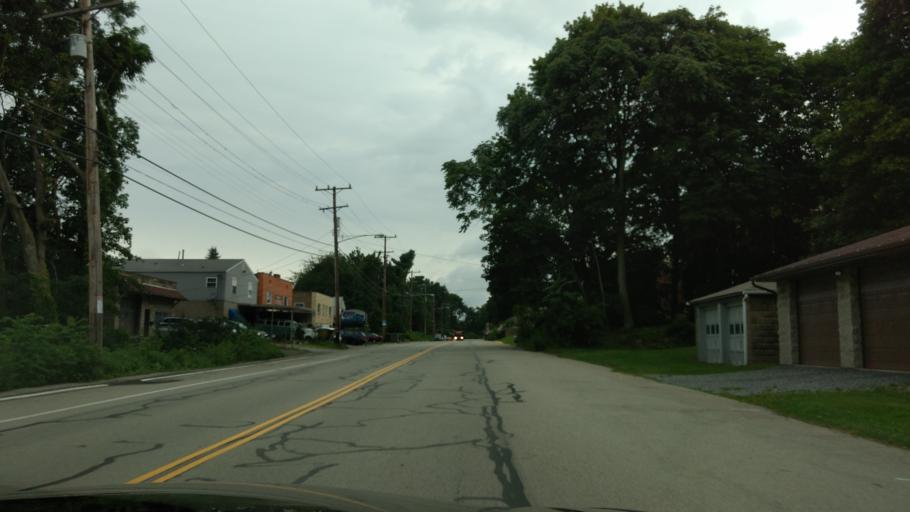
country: US
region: Pennsylvania
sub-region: Allegheny County
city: West View
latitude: 40.5158
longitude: -80.0446
